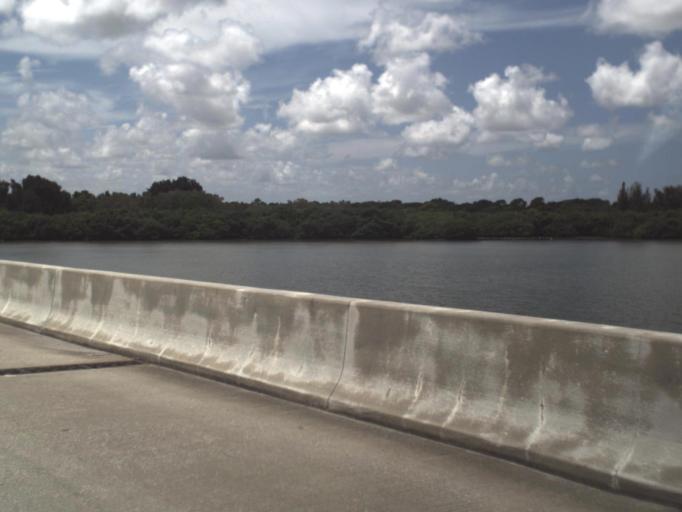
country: US
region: Florida
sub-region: Pinellas County
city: South Highpoint
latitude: 27.9269
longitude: -82.6997
